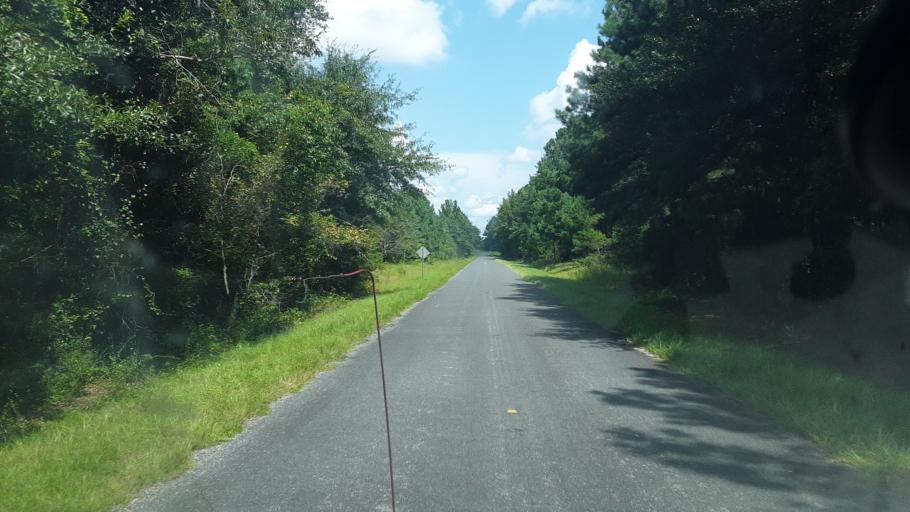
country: US
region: South Carolina
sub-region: Calhoun County
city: Oak Grove
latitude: 33.6672
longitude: -80.9729
